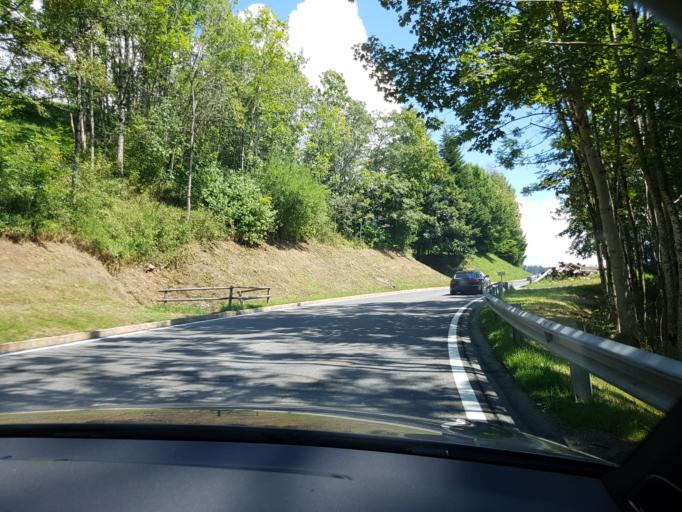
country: AT
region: Vorarlberg
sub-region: Politischer Bezirk Bregenz
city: Damuels
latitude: 47.2457
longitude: 9.9109
